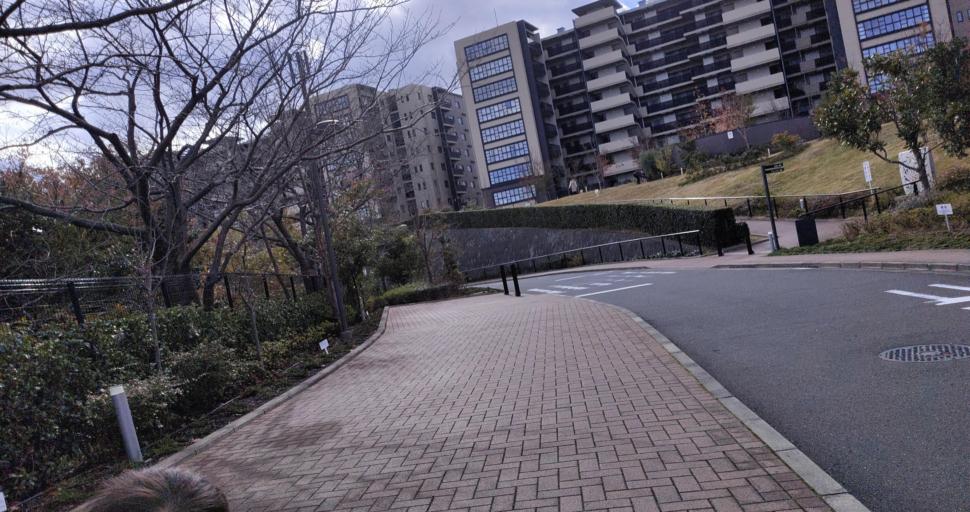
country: JP
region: Kanagawa
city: Yokohama
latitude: 35.4024
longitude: 139.6131
